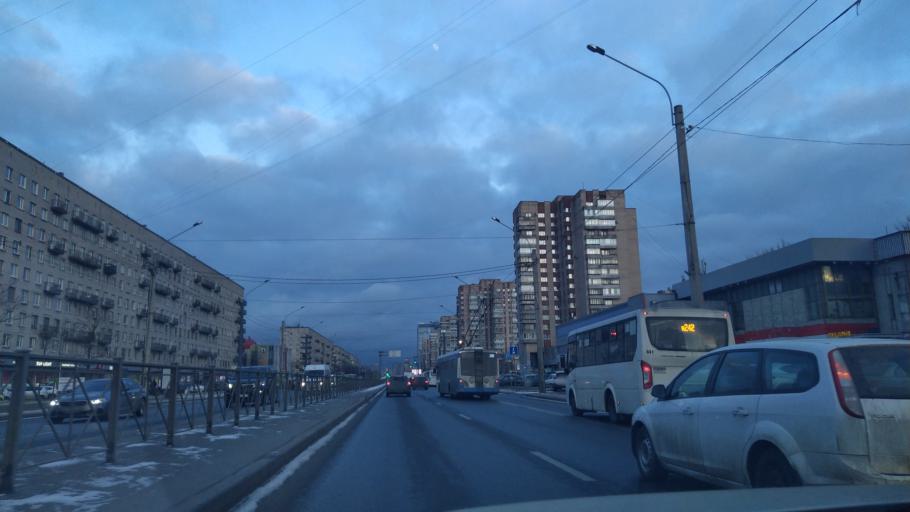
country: RU
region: St.-Petersburg
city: Dachnoye
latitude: 59.8519
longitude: 30.2631
